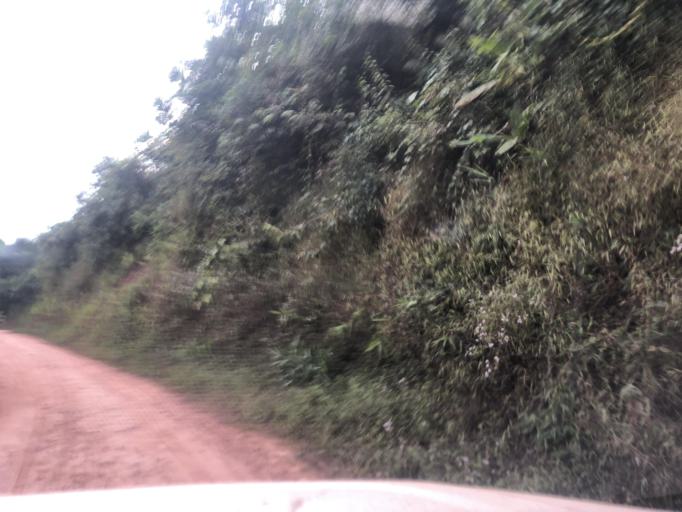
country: CN
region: Yunnan
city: Menglie
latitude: 22.1184
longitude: 101.7336
